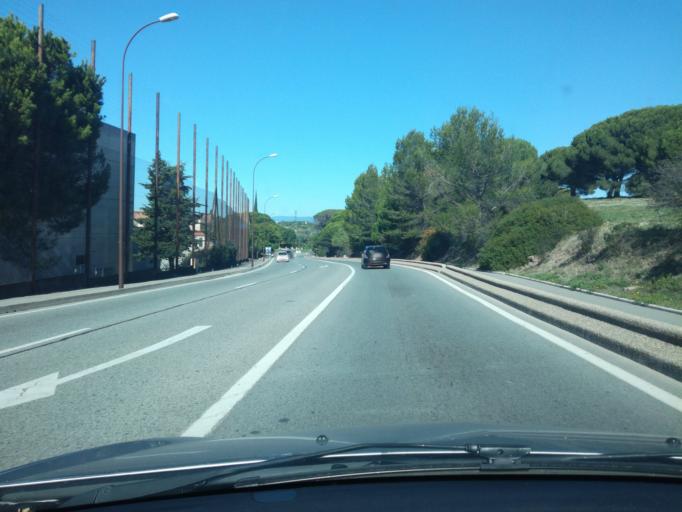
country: FR
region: Provence-Alpes-Cote d'Azur
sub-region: Departement du Var
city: Frejus
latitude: 43.4415
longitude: 6.7422
